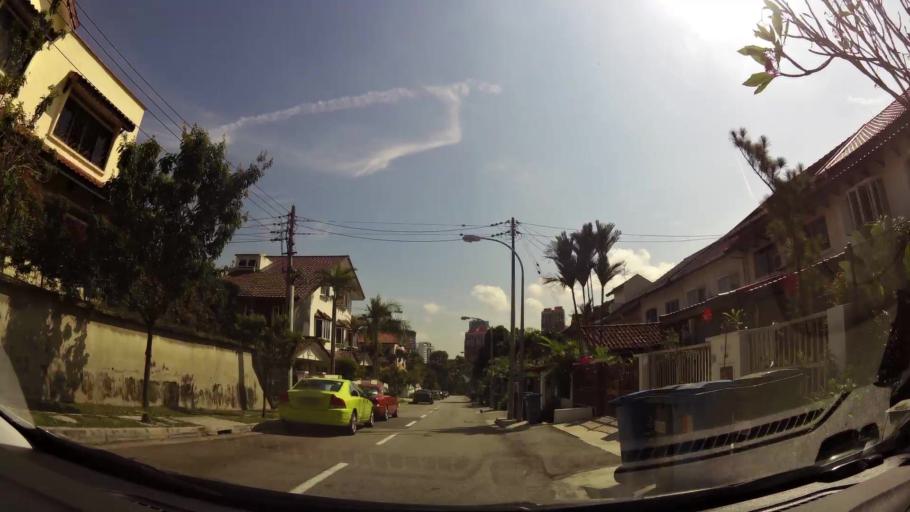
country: SG
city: Singapore
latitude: 1.3581
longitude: 103.8257
